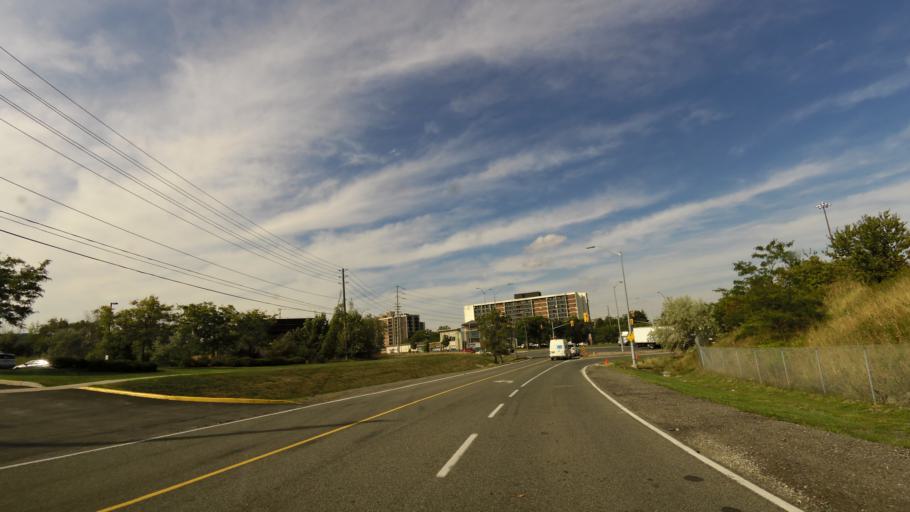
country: CA
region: Ontario
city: Mississauga
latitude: 43.5247
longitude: -79.6502
